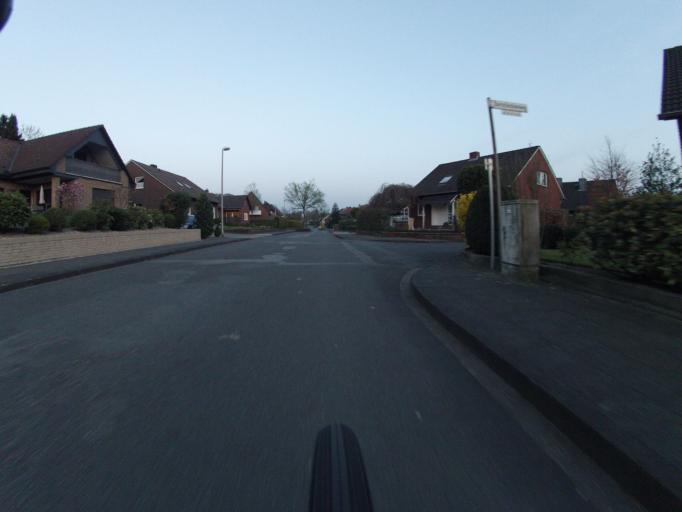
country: DE
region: North Rhine-Westphalia
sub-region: Regierungsbezirk Munster
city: Mettingen
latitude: 52.2709
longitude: 7.7796
